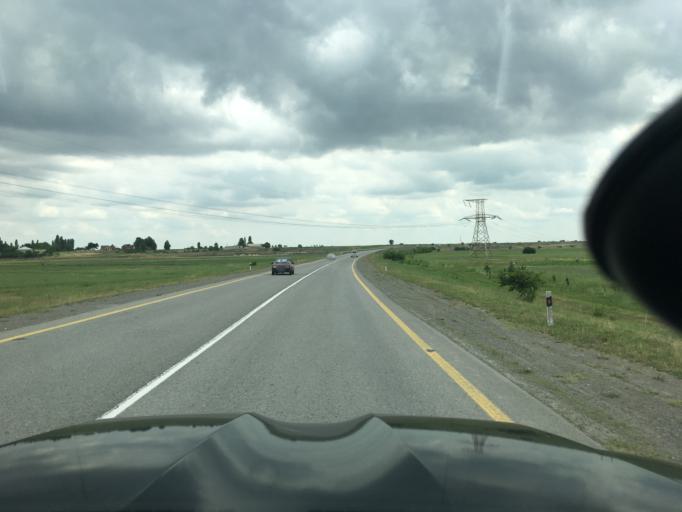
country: AZ
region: Tovuz
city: Qaraxanli
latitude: 41.0289
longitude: 45.6179
